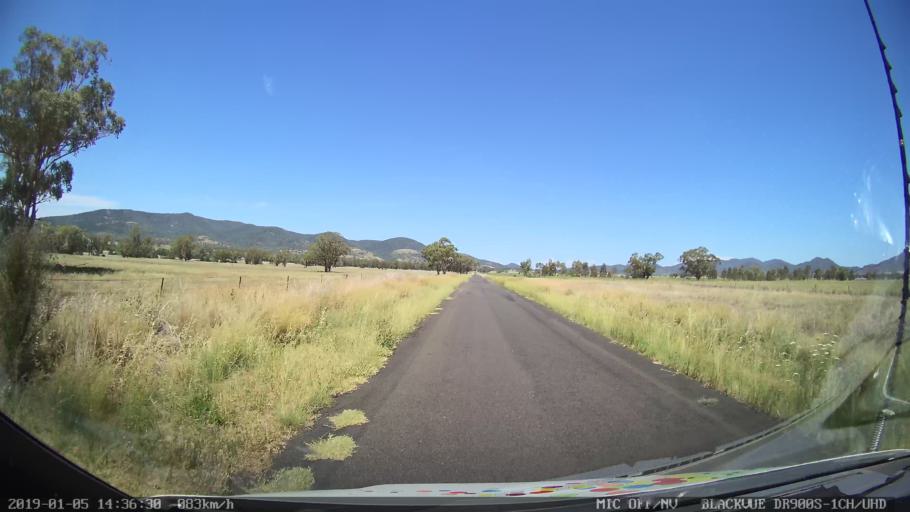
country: AU
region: New South Wales
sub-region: Tamworth Municipality
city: Phillip
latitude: -31.2449
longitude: 150.6650
